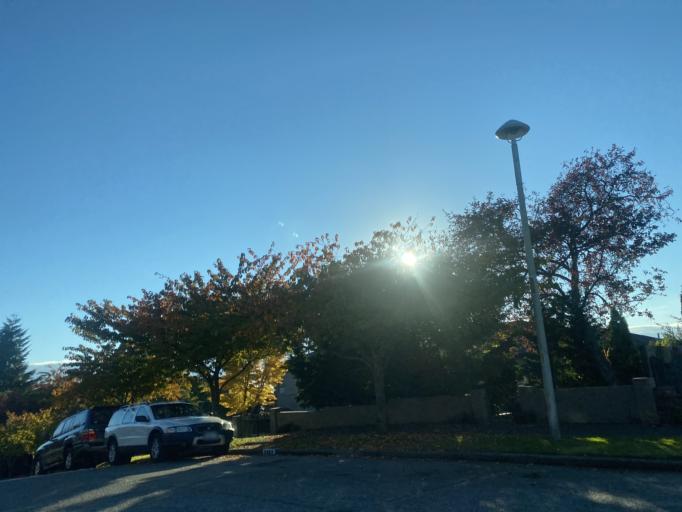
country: US
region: Washington
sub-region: King County
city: Seattle
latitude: 47.6468
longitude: -122.4119
